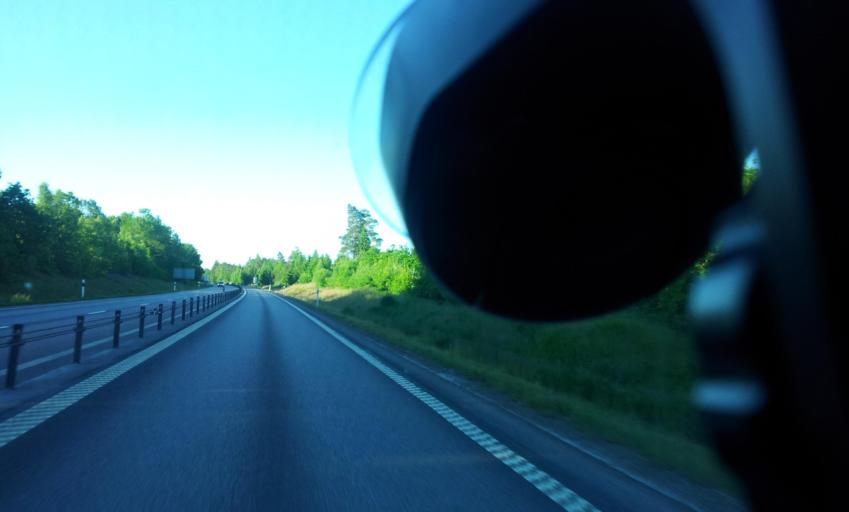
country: SE
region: Kalmar
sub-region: Oskarshamns Kommun
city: Paskallavik
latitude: 57.1936
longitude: 16.4384
